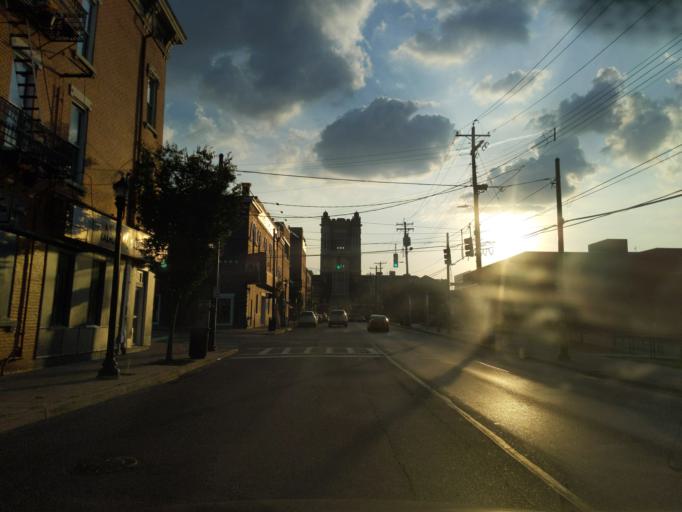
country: US
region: Ohio
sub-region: Hamilton County
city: Saint Bernard
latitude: 39.1285
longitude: -84.5188
